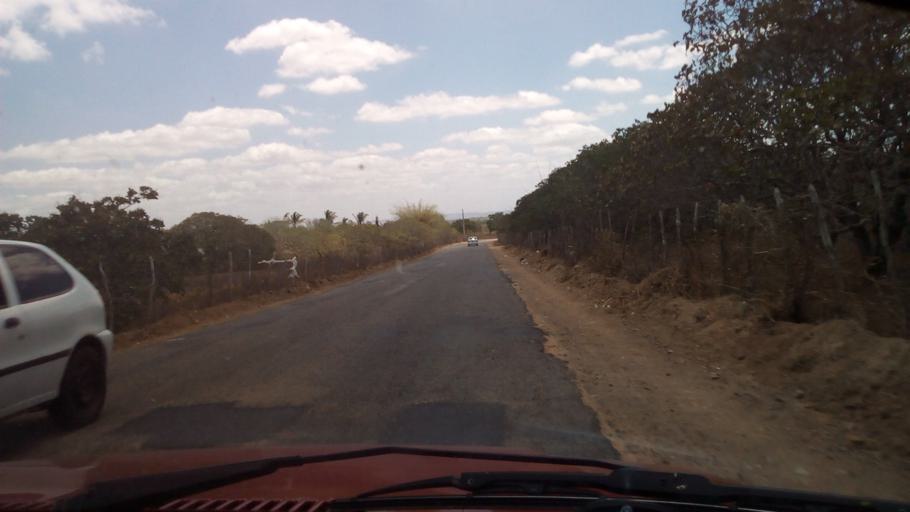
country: BR
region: Paraiba
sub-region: Cacimba De Dentro
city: Cacimba de Dentro
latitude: -6.5902
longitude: -35.8157
